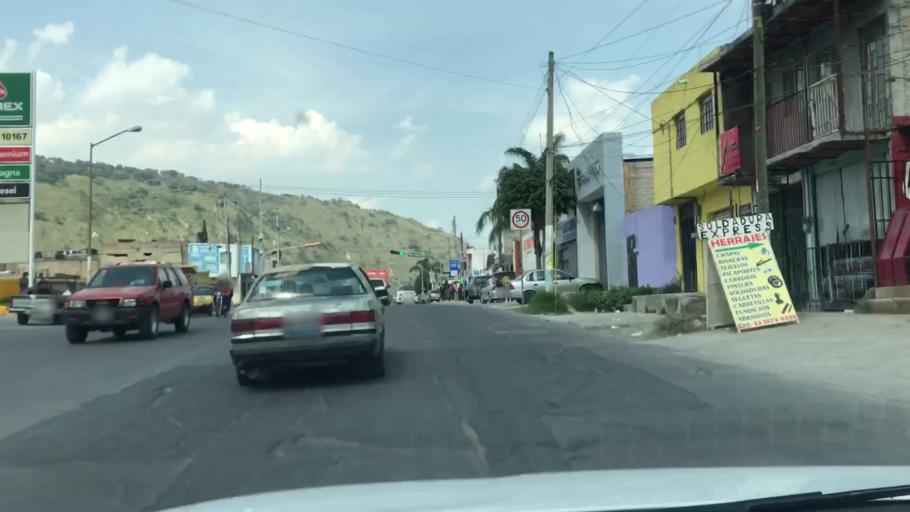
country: MX
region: Jalisco
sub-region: Tlajomulco de Zuniga
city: Palomar
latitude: 20.6413
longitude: -103.4611
